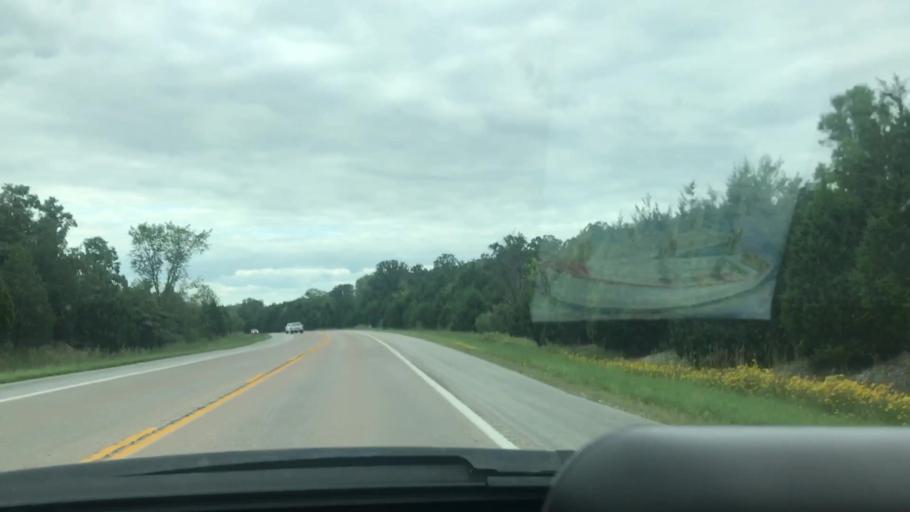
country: US
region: Missouri
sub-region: Benton County
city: Warsaw
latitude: 38.2023
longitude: -93.3260
